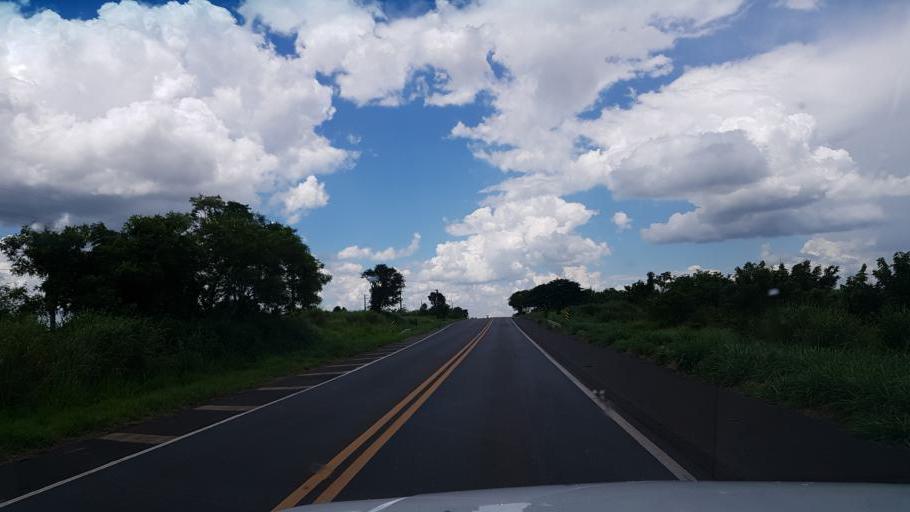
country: BR
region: Sao Paulo
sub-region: Paraguacu Paulista
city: Paraguacu Paulista
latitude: -22.3790
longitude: -50.6197
